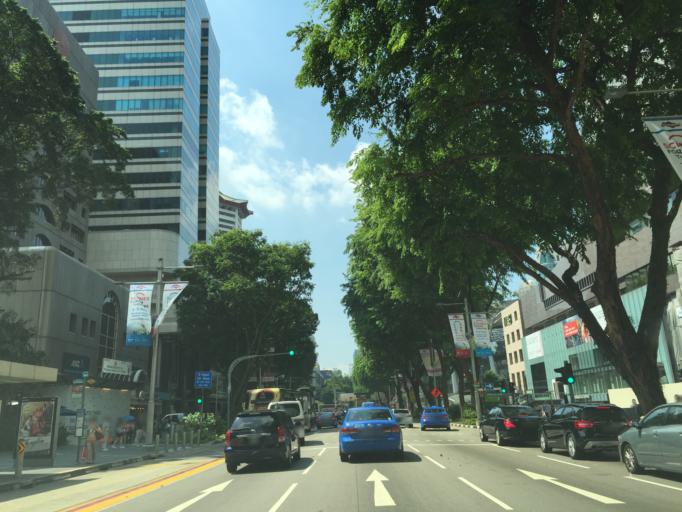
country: SG
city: Singapore
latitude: 1.3059
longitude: 103.8302
